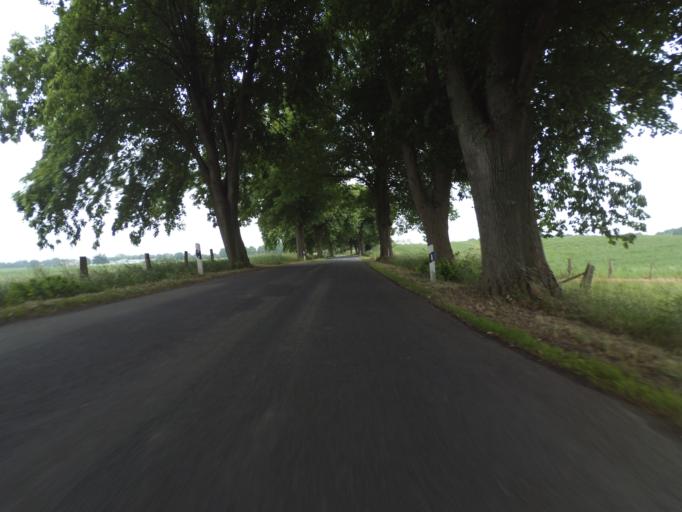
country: DE
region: Mecklenburg-Vorpommern
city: Lubz
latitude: 53.5085
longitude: 12.0015
